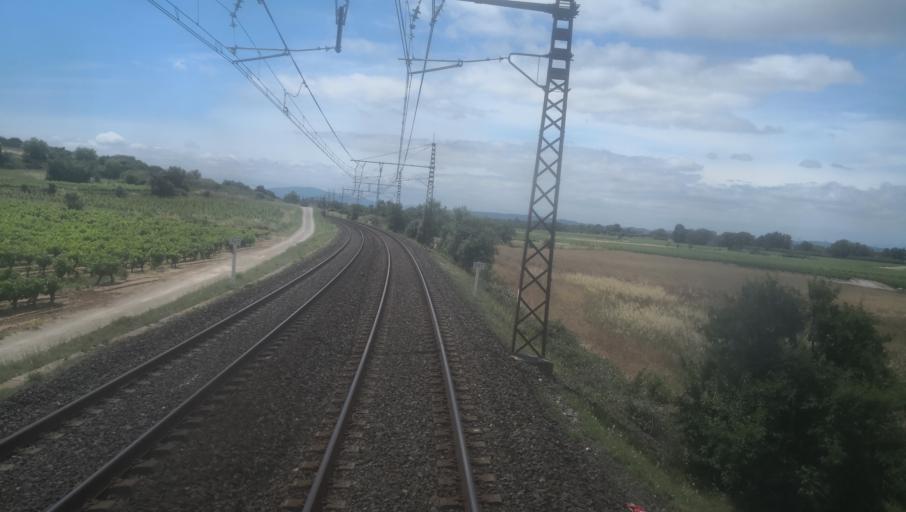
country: FR
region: Languedoc-Roussillon
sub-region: Departement de l'Aude
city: Nevian
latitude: 43.2132
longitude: 2.8847
